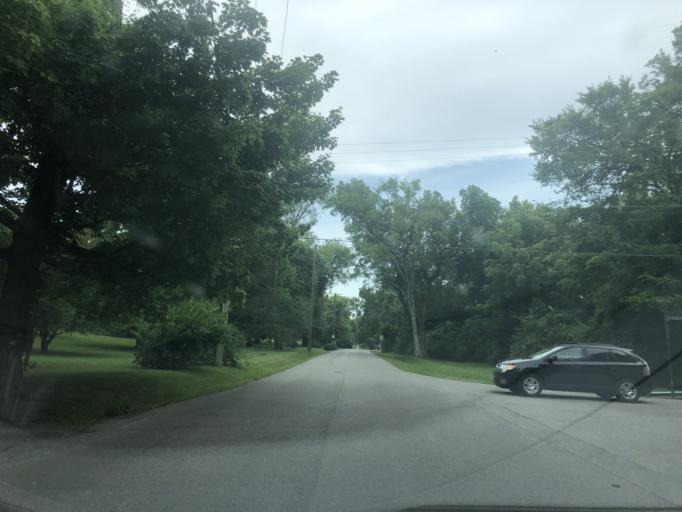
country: US
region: Tennessee
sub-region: Davidson County
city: Oak Hill
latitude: 36.1002
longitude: -86.7771
